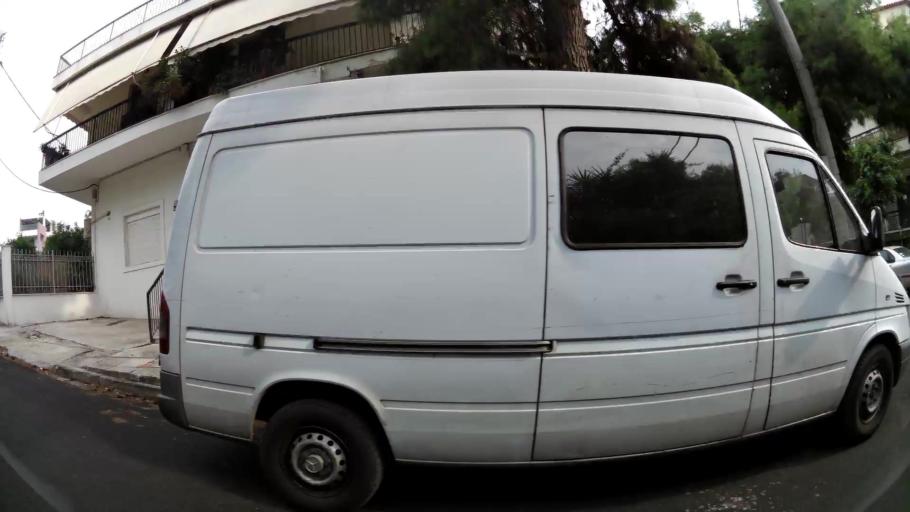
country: GR
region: Attica
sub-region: Nomarchia Athinas
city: Agios Dimitrios
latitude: 37.9209
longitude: 23.7361
